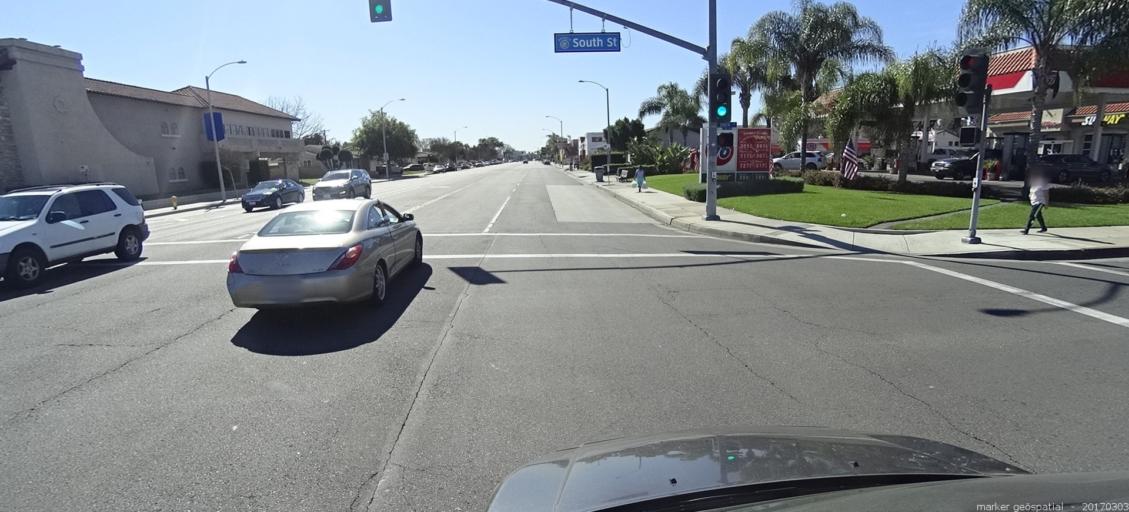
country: US
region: California
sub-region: Orange County
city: Anaheim
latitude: 33.8255
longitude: -117.9168
